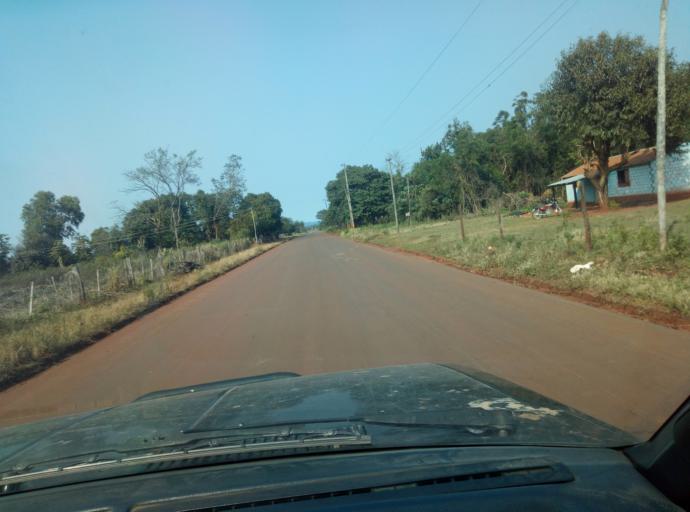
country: PY
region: Caaguazu
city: Carayao
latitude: -25.2146
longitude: -56.2886
